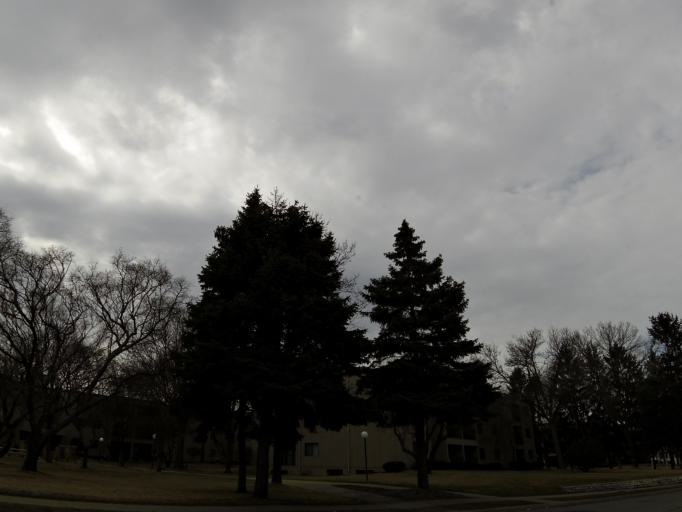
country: US
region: Minnesota
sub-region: Hennepin County
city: Edina
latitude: 44.8683
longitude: -93.3316
